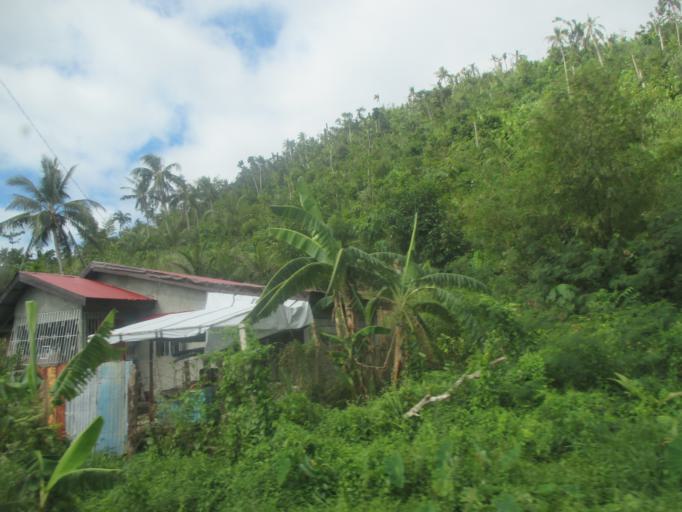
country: PH
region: Eastern Visayas
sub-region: Province of Eastern Samar
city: Lawa-an
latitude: 11.1102
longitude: 125.2453
